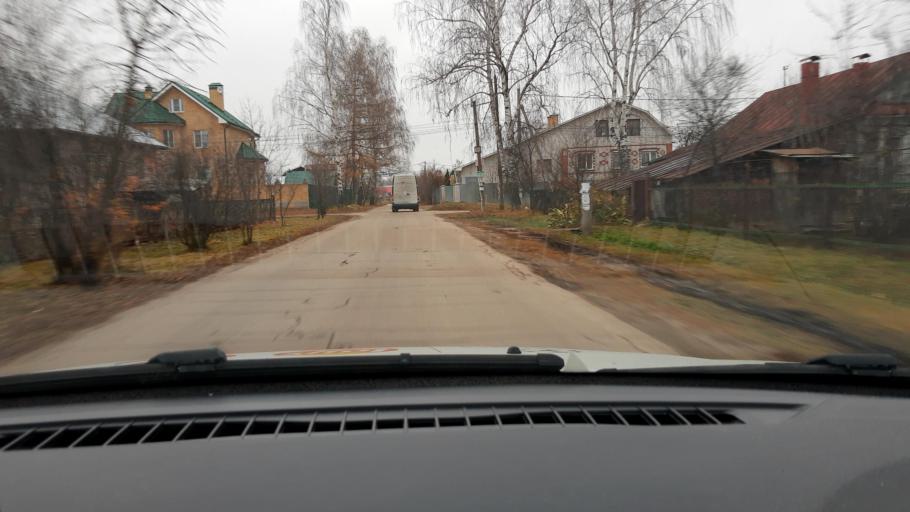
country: RU
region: Nizjnij Novgorod
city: Burevestnik
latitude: 56.2020
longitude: 43.7765
